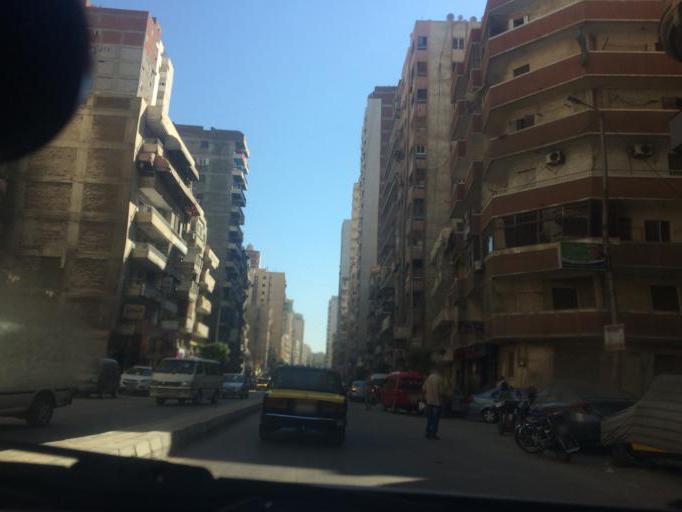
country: EG
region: Alexandria
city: Alexandria
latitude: 31.2768
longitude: 30.0084
